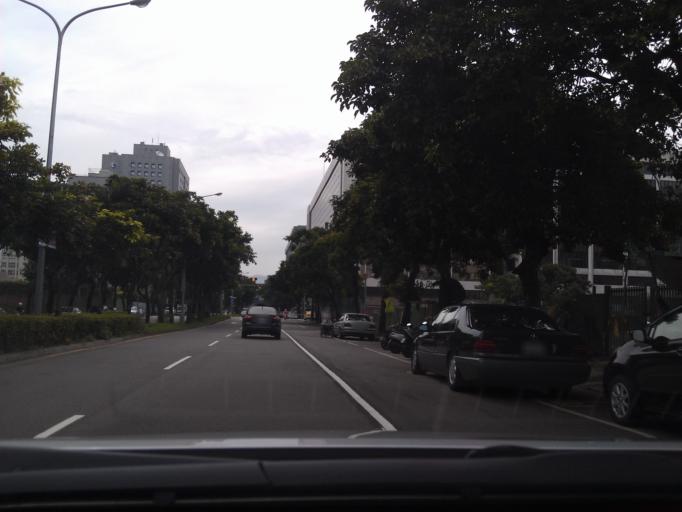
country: TW
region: Taipei
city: Taipei
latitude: 25.0322
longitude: 121.5229
